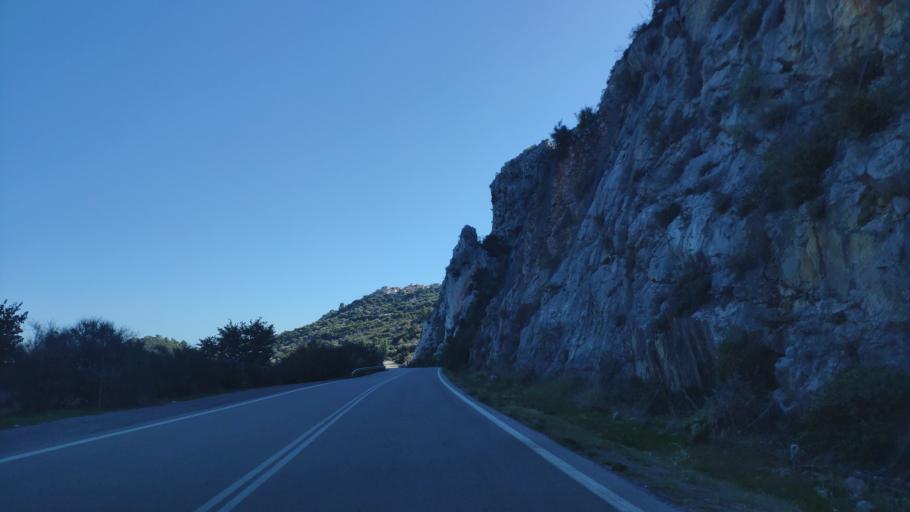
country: GR
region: Peloponnese
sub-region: Nomos Argolidos
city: Palaia Epidavros
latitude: 37.5824
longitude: 23.2328
